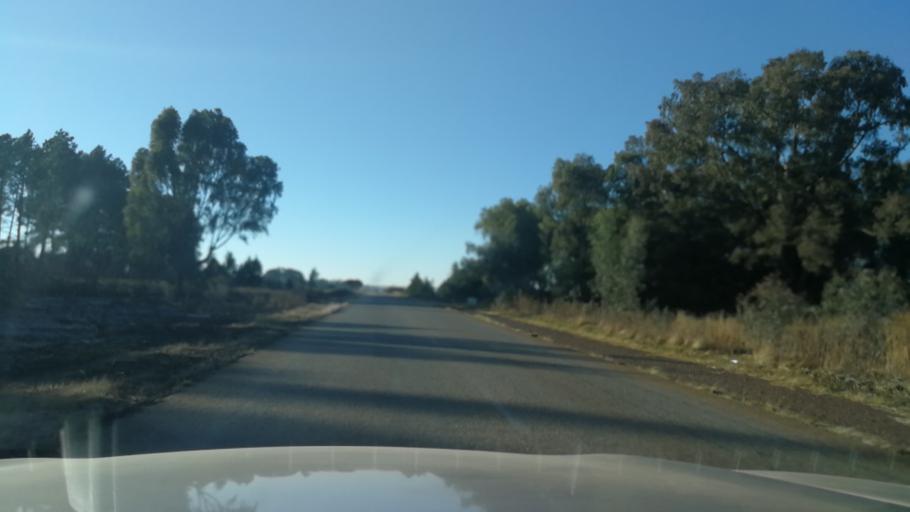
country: ZA
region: North-West
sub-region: Bojanala Platinum District Municipality
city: Rustenburg
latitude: -25.9532
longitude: 27.1855
